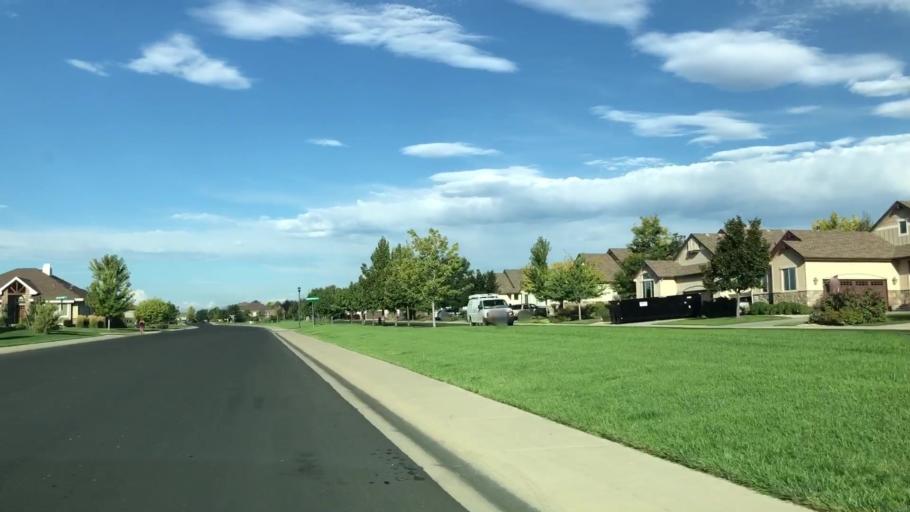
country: US
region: Colorado
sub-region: Weld County
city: Windsor
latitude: 40.4616
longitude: -104.9730
